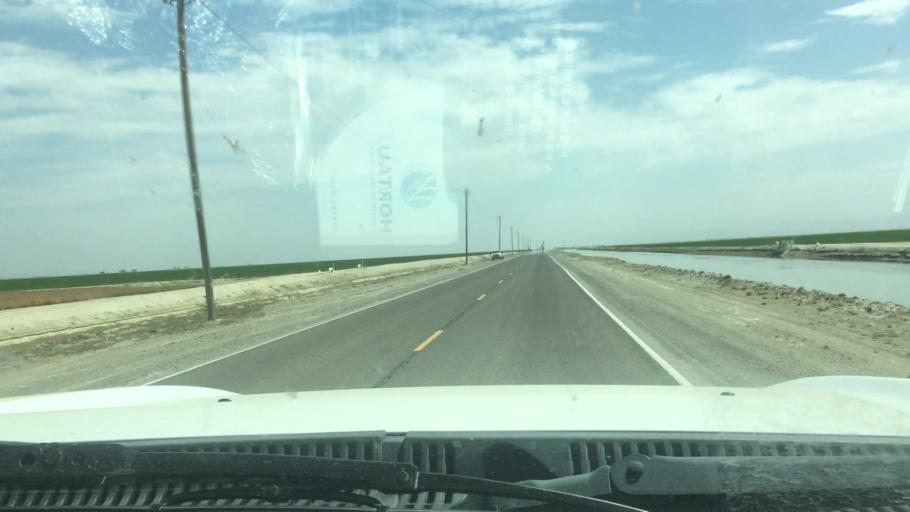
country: US
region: California
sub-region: Tulare County
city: Alpaugh
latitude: 35.8995
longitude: -119.5734
